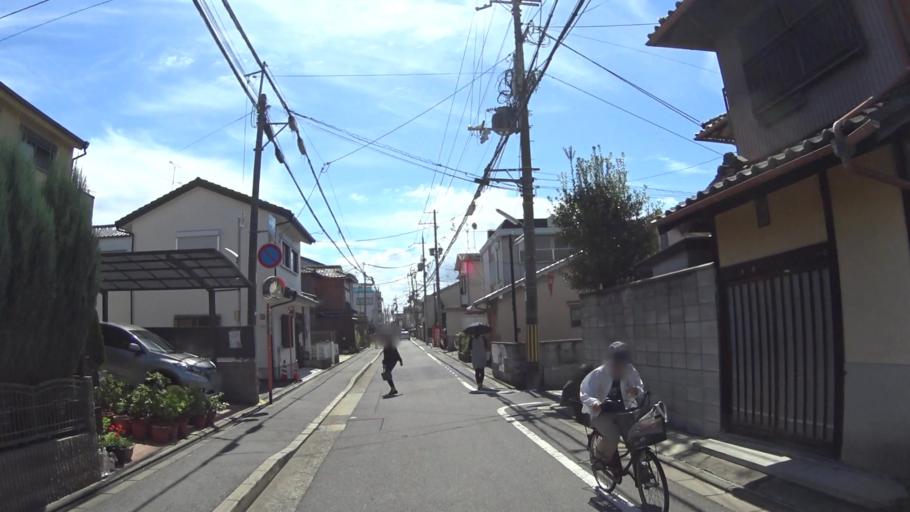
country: JP
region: Kyoto
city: Uji
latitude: 34.9413
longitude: 135.7651
